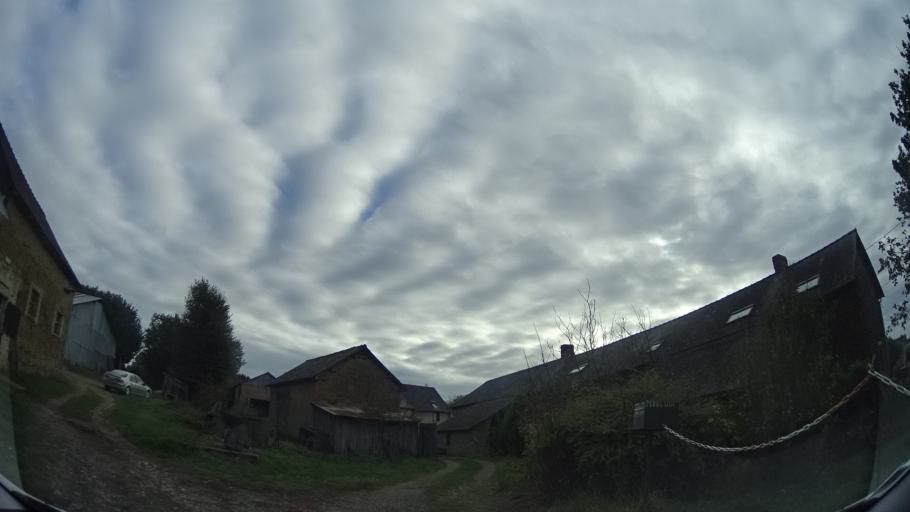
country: FR
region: Brittany
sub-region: Departement d'Ille-et-Vilaine
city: Vignoc
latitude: 48.2347
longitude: -1.7856
